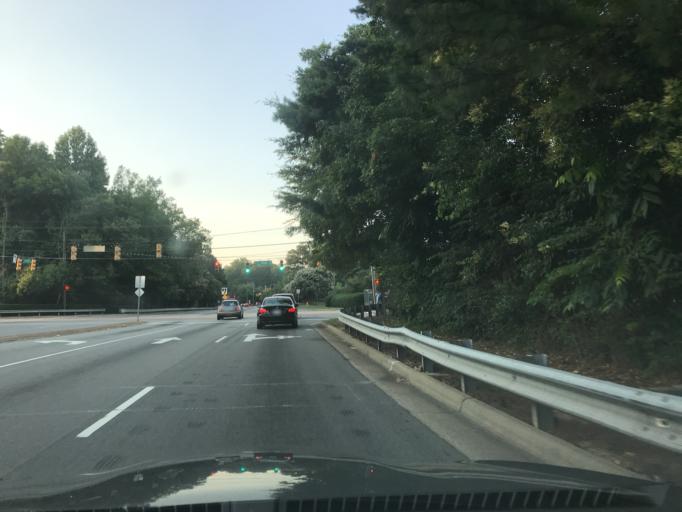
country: US
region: North Carolina
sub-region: Wake County
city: Raleigh
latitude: 35.7772
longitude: -78.6141
